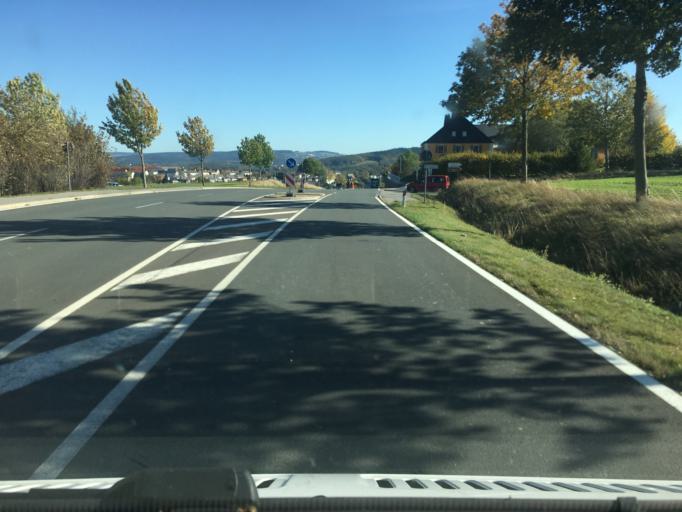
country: DE
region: Saxony
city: Schneeberg
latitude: 50.6015
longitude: 12.6146
